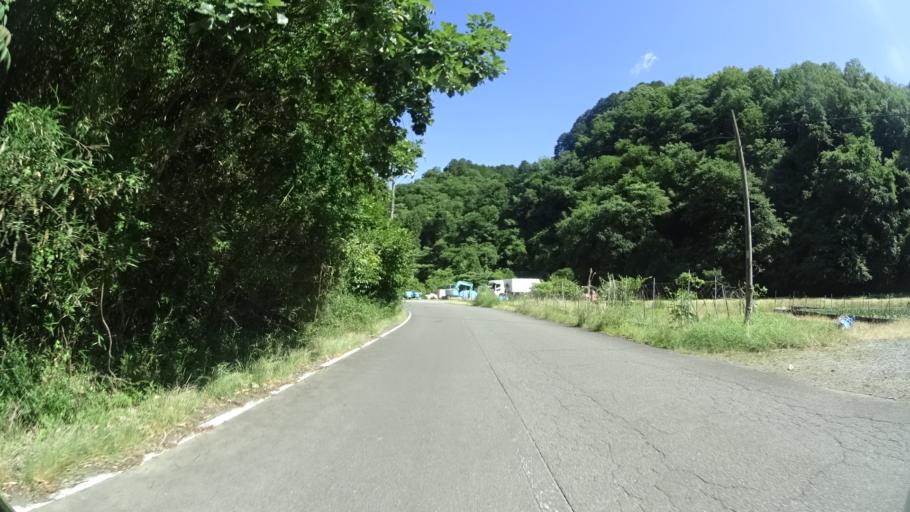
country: JP
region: Kyoto
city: Fukuchiyama
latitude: 35.3606
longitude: 135.1050
